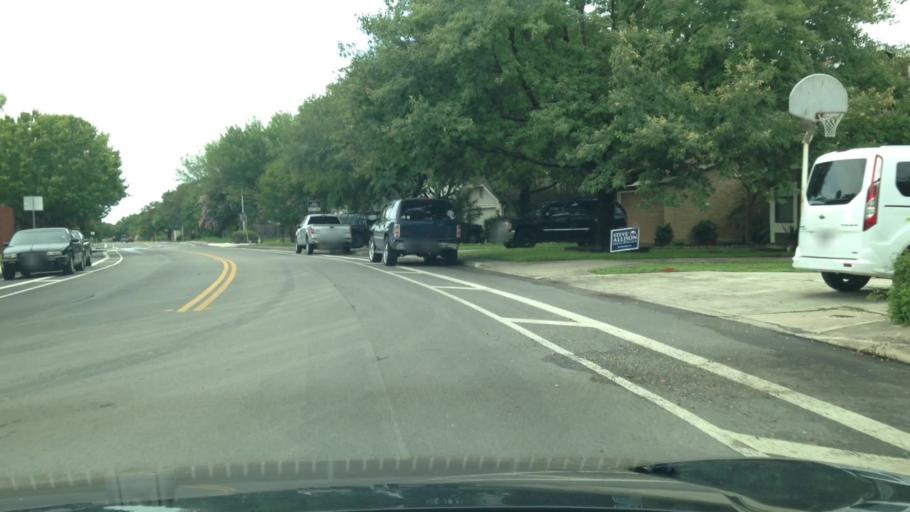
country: US
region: Texas
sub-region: Bexar County
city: Hollywood Park
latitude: 29.5753
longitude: -98.4253
